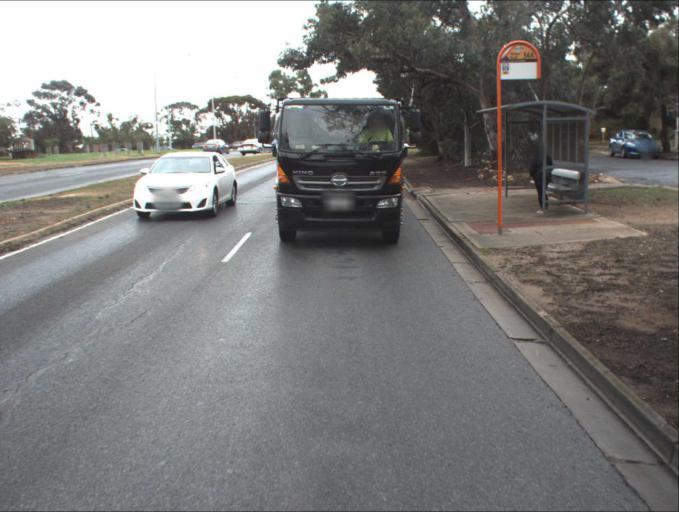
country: AU
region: South Australia
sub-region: Salisbury
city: Ingle Farm
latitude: -34.8369
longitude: 138.6455
